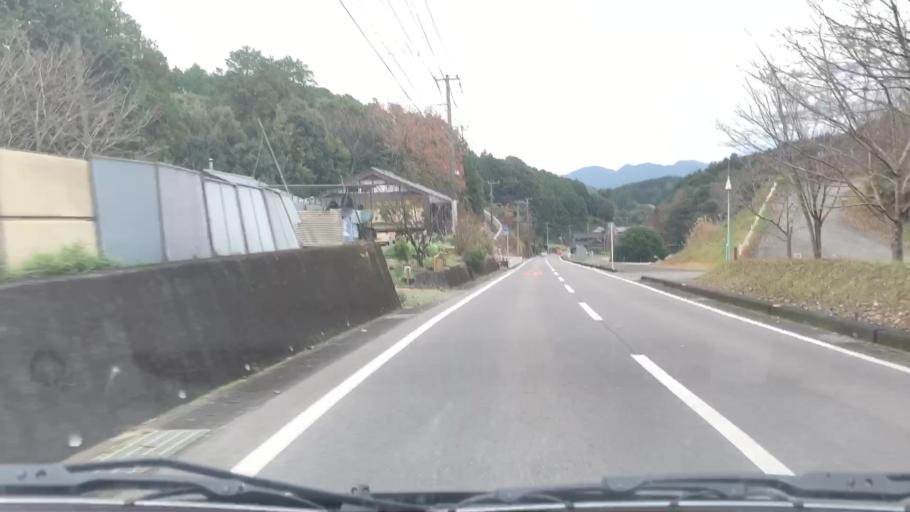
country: JP
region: Saga Prefecture
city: Ureshinomachi-shimojuku
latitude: 33.1304
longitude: 129.9766
